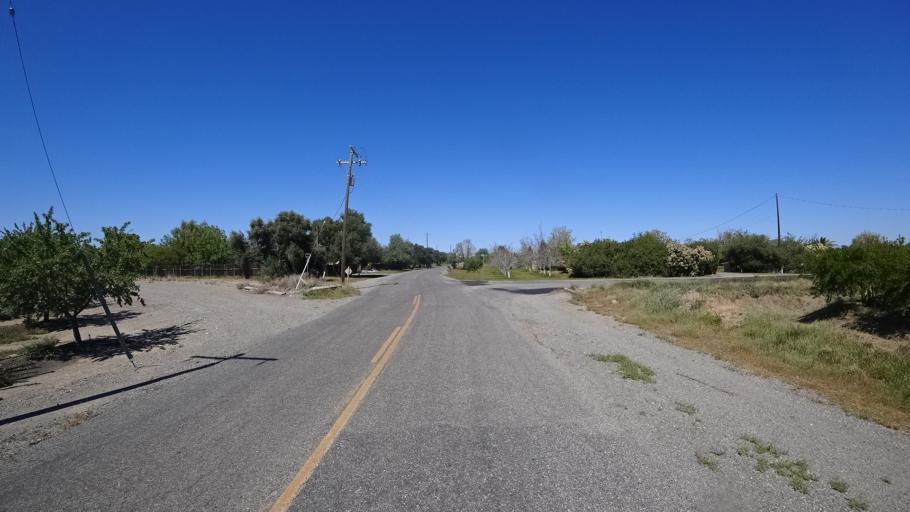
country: US
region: California
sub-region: Glenn County
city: Orland
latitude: 39.7394
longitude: -122.1594
